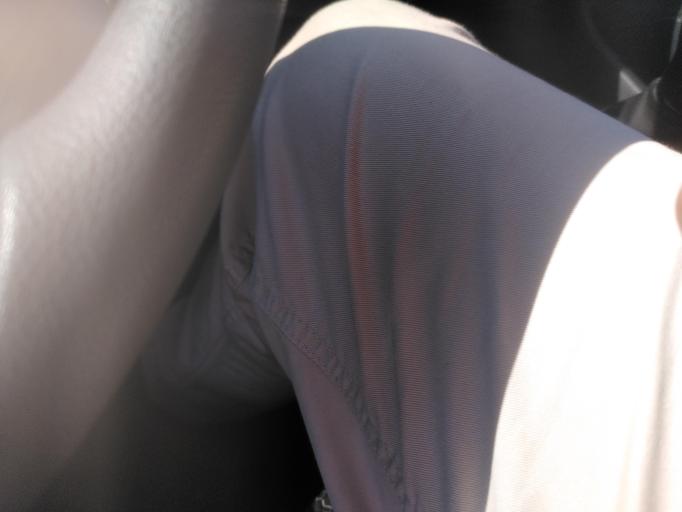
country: FR
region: Alsace
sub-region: Departement du Haut-Rhin
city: Kunheim
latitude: 48.0992
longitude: 7.5808
